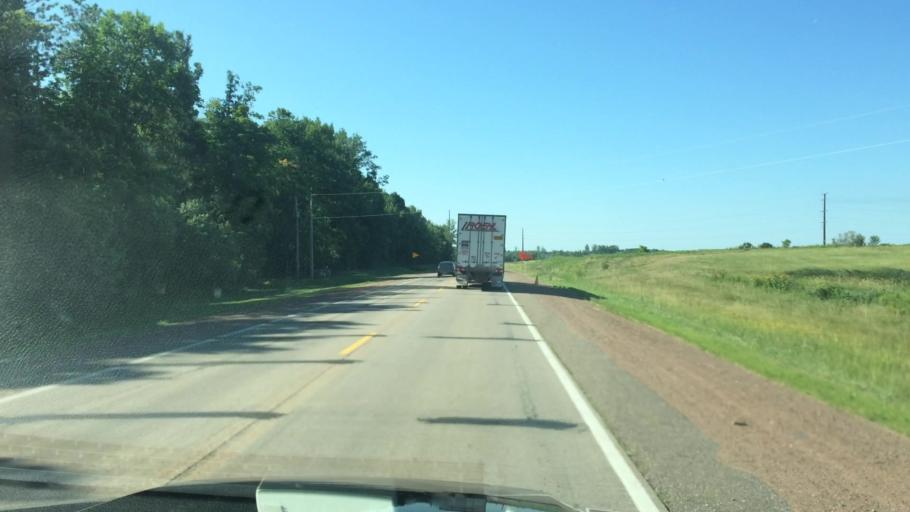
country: US
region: Wisconsin
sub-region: Marathon County
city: Athens
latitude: 44.9396
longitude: -90.0791
